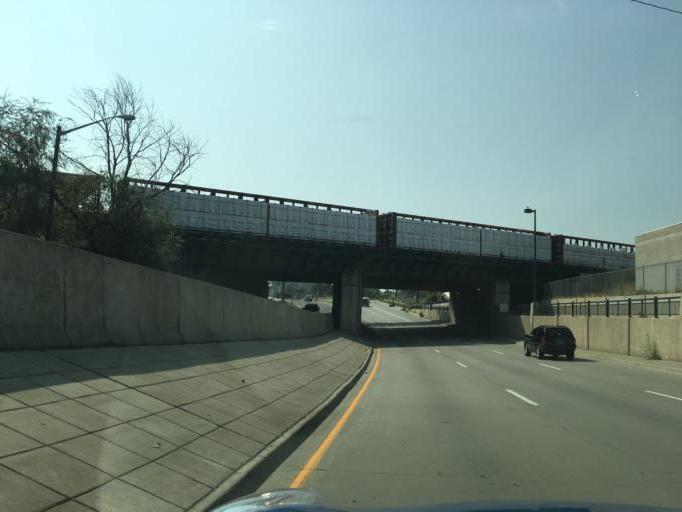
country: US
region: Colorado
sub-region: Denver County
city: Denver
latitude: 39.7776
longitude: -104.9793
